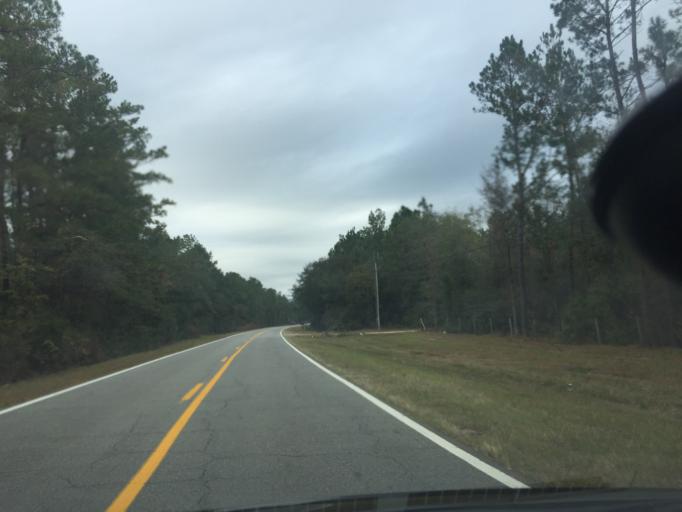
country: US
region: Georgia
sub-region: Chatham County
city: Bloomingdale
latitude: 32.0980
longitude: -81.3800
